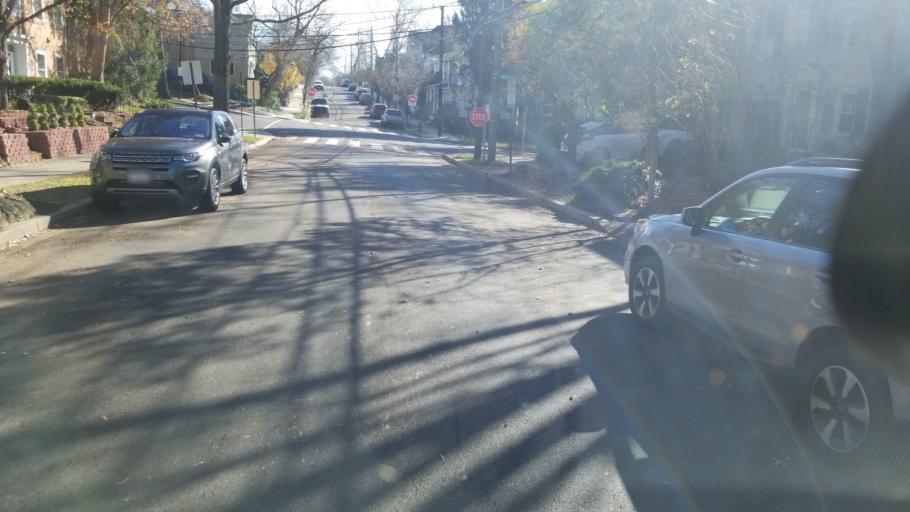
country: US
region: Maryland
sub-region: Montgomery County
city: Brookmont
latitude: 38.9276
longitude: -77.1058
